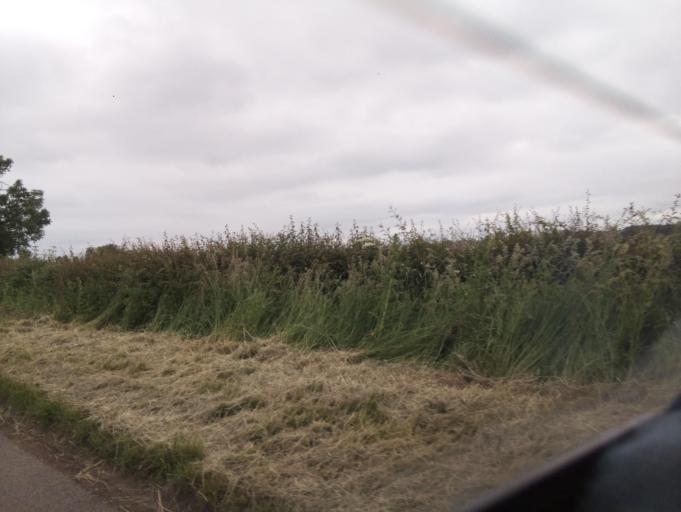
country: GB
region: England
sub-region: Leicestershire
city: Melton Mowbray
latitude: 52.7048
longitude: -0.8344
